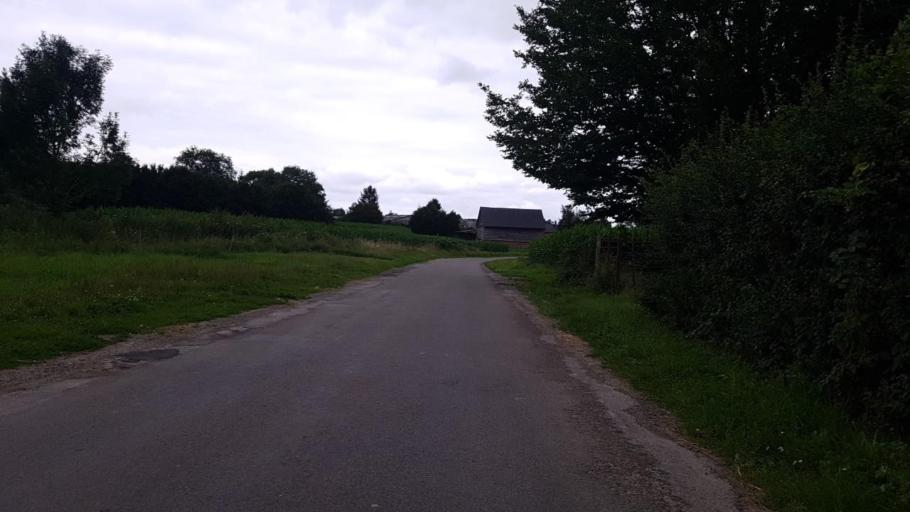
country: FR
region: Picardie
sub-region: Departement de l'Aisne
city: La Capelle
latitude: 49.9051
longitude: 3.8889
